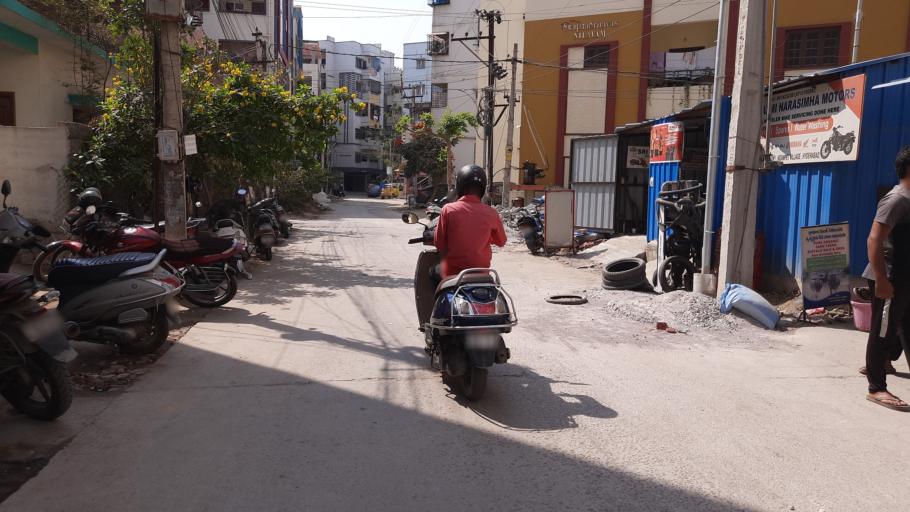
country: IN
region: Telangana
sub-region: Rangareddi
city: Kukatpalli
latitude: 17.5150
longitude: 78.3800
